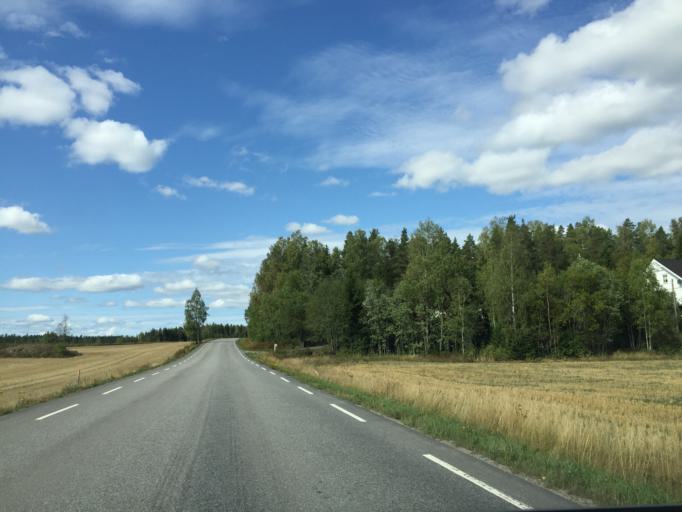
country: NO
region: Ostfold
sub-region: Hobol
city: Elvestad
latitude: 59.6042
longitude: 10.9074
